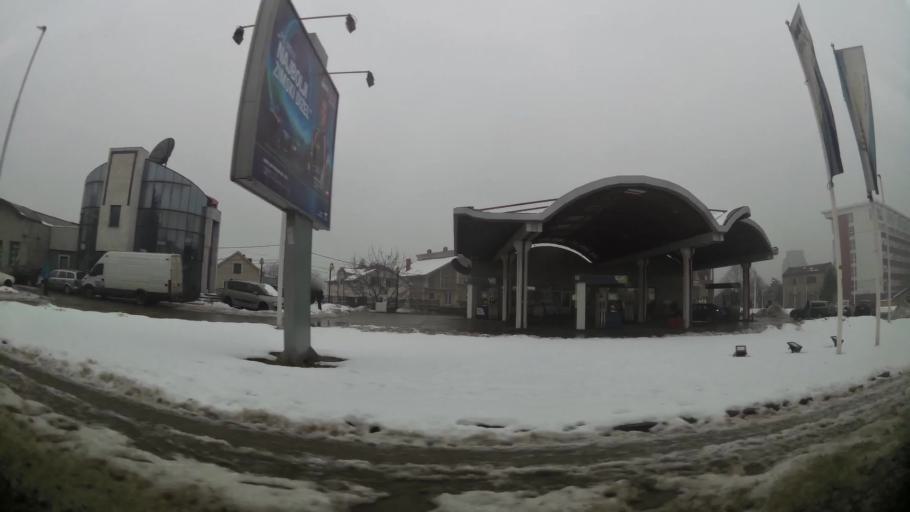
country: RS
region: Central Serbia
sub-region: Belgrade
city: Zvezdara
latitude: 44.7823
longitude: 20.5224
